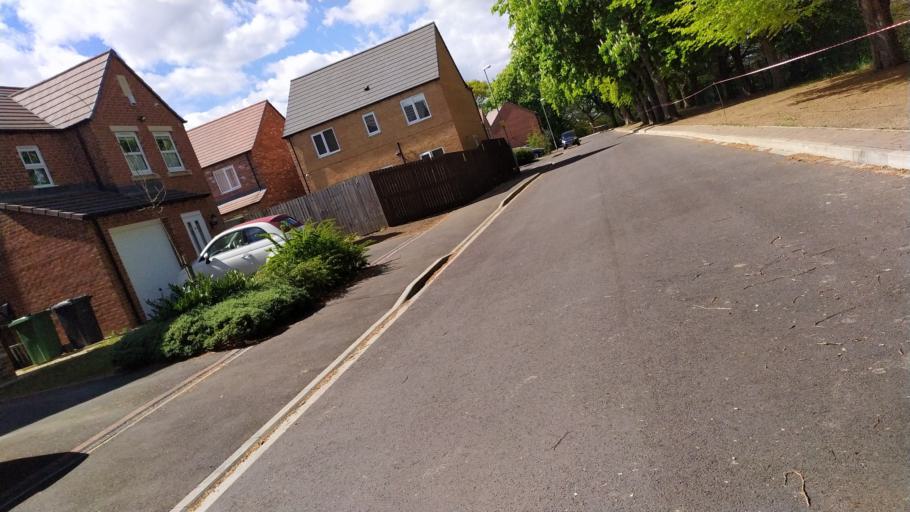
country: GB
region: England
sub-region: City and Borough of Leeds
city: Shadwell
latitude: 53.8098
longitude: -1.4783
